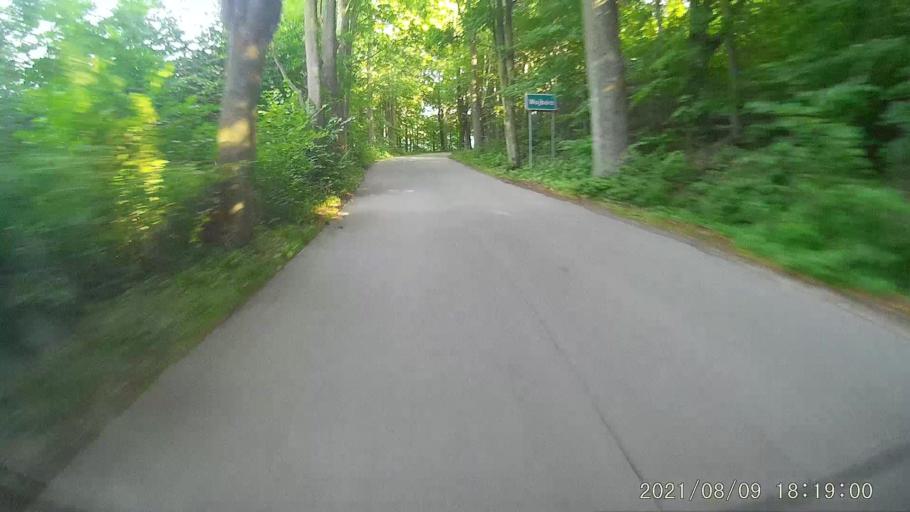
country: PL
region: Lower Silesian Voivodeship
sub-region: Powiat zabkowicki
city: Bardo
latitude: 50.5092
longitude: 16.6827
